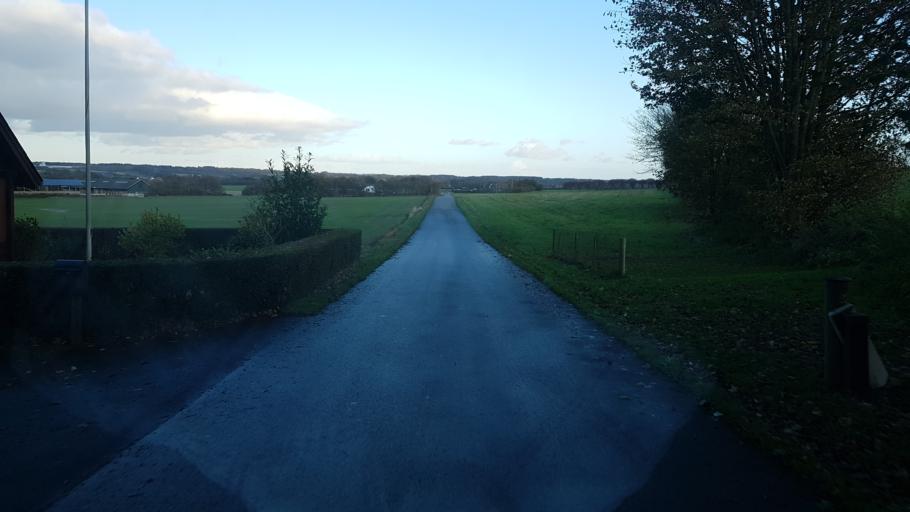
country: DK
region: South Denmark
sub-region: Vejen Kommune
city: Brorup
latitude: 55.4565
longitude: 8.9780
